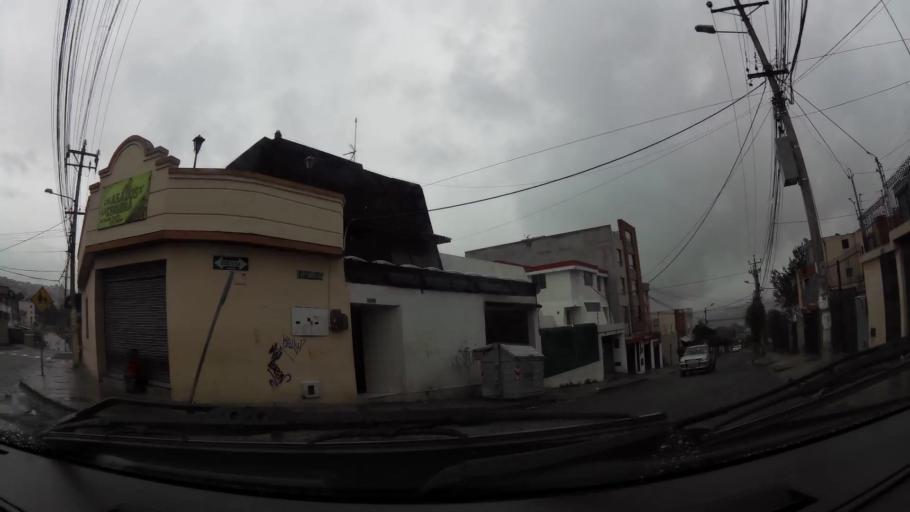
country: EC
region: Pichincha
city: Quito
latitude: -0.1080
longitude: -78.5016
